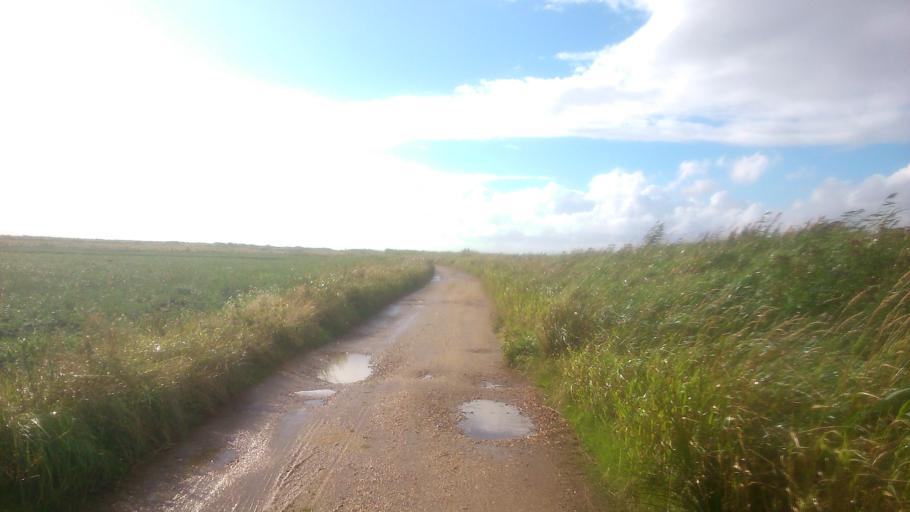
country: DK
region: Central Jutland
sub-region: Ringkobing-Skjern Kommune
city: Skjern
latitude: 55.9184
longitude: 8.4870
